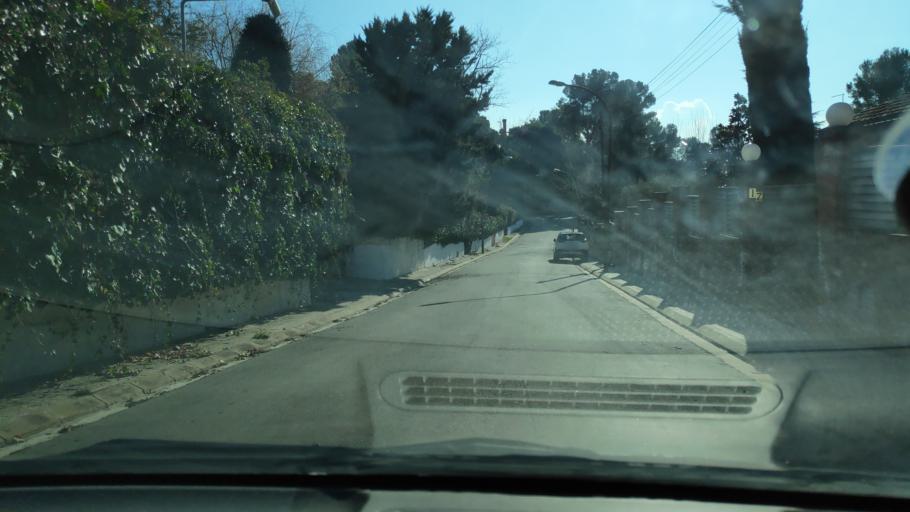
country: ES
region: Catalonia
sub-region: Provincia de Barcelona
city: Sant Quirze del Valles
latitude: 41.5006
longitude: 2.0786
